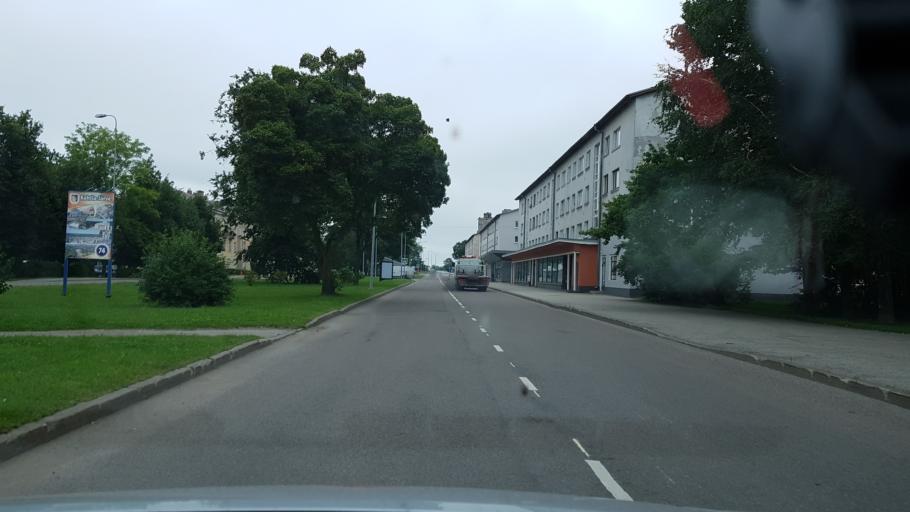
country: EE
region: Ida-Virumaa
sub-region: Kohtla-Jaerve linn
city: Kohtla-Jarve
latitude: 59.4006
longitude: 27.2900
